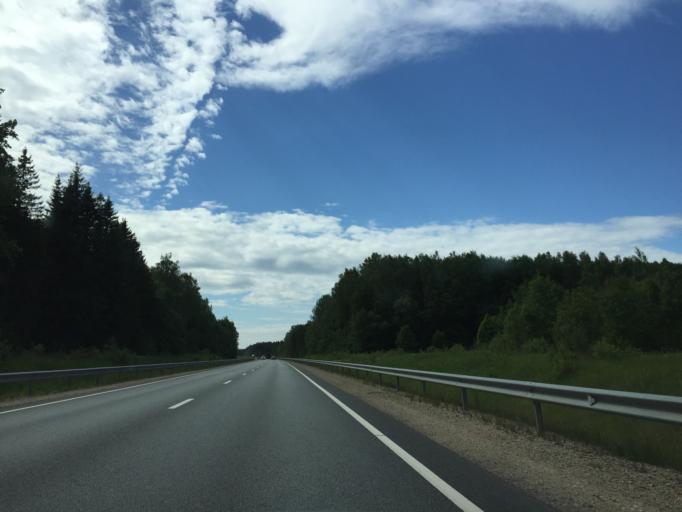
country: LV
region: Ogre
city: Jumprava
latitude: 56.7999
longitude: 24.9442
